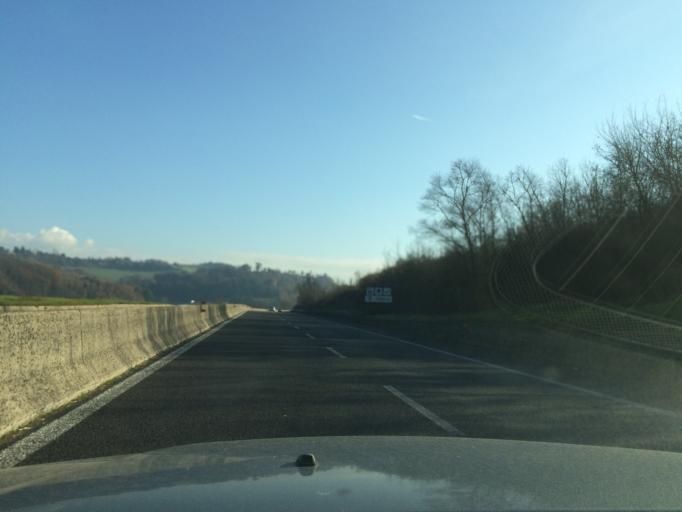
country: IT
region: Umbria
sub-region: Provincia di Perugia
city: Todi
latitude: 42.7802
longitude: 12.4408
